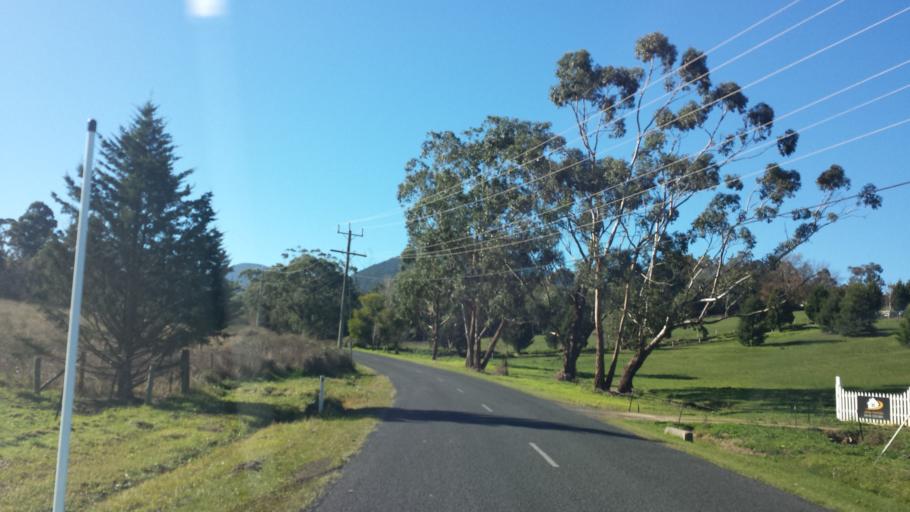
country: AU
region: Victoria
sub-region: Yarra Ranges
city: Healesville
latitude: -37.6710
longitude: 145.5208
